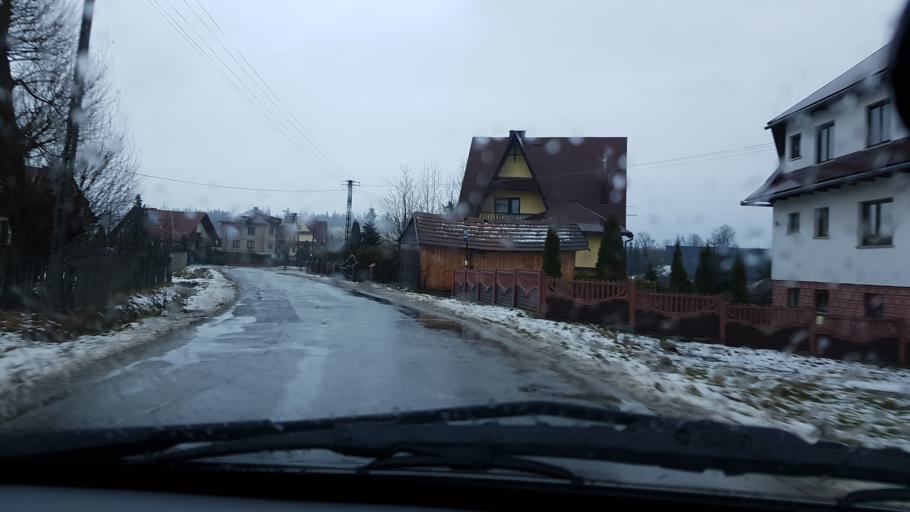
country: PL
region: Lesser Poland Voivodeship
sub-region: Powiat nowotarski
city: Lasek
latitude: 49.4971
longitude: 19.9486
